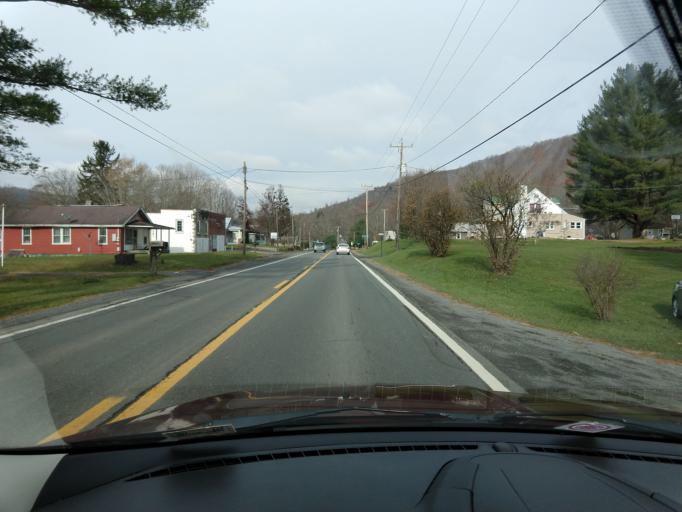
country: US
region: West Virginia
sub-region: Greenbrier County
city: Rainelle
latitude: 37.9823
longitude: -80.7166
